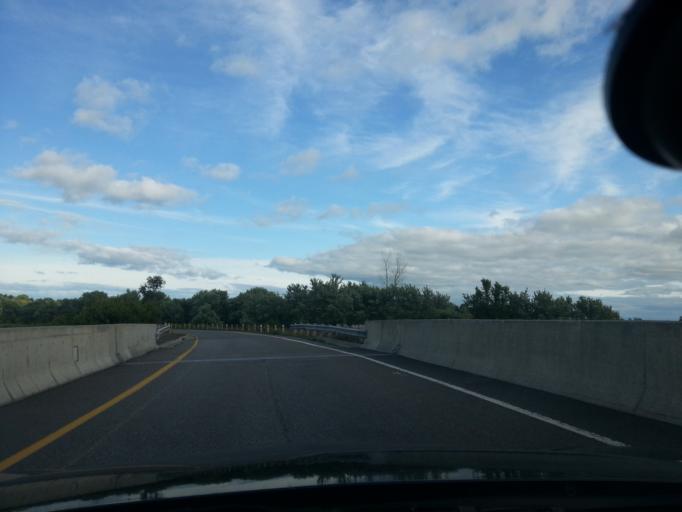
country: CA
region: Ontario
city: Hawkesbury
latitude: 45.5651
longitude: -74.5044
